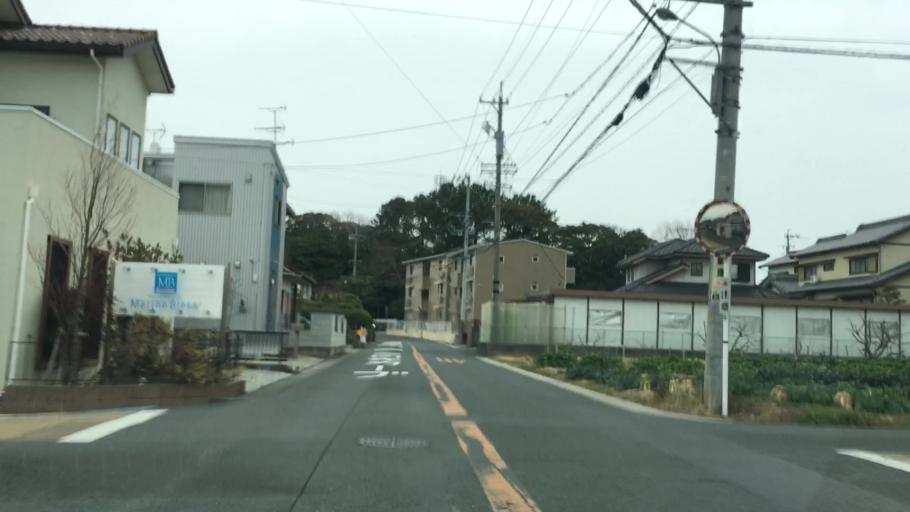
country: JP
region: Aichi
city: Toyohashi
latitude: 34.7396
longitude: 137.3692
